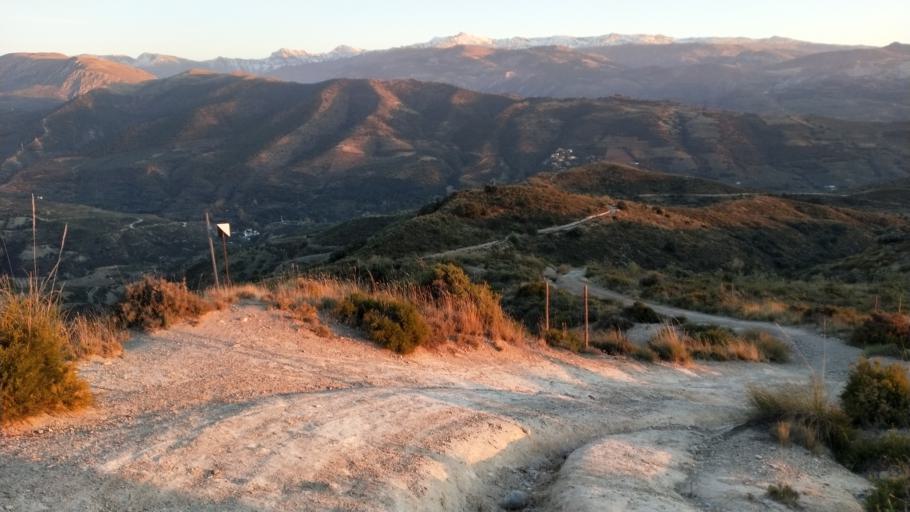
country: ES
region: Andalusia
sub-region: Provincia de Granada
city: Dudar
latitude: 37.1974
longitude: -3.5026
